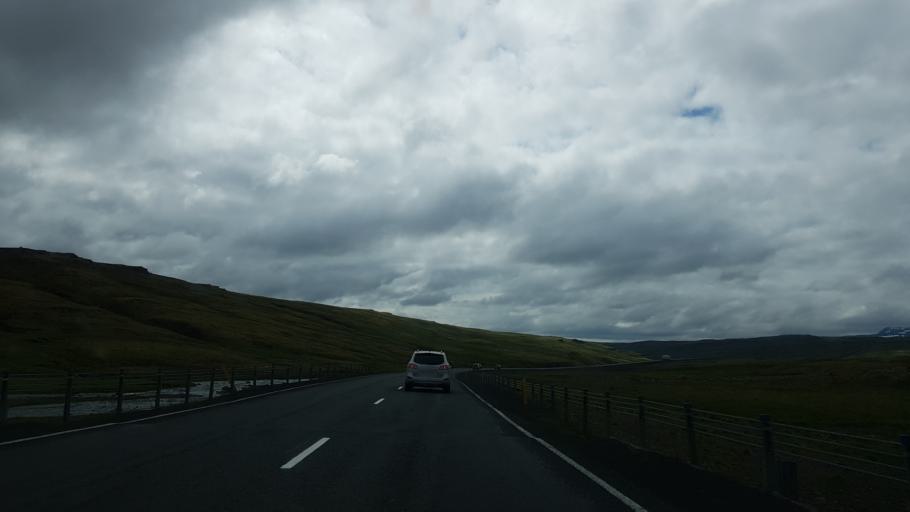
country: IS
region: West
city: Borgarnes
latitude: 64.9146
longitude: -21.1419
